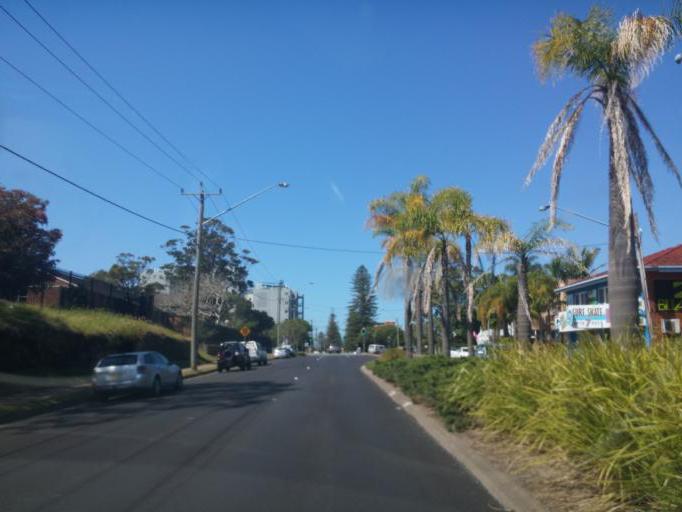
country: AU
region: New South Wales
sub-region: Port Macquarie-Hastings
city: Port Macquarie
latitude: -31.4309
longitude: 152.9134
